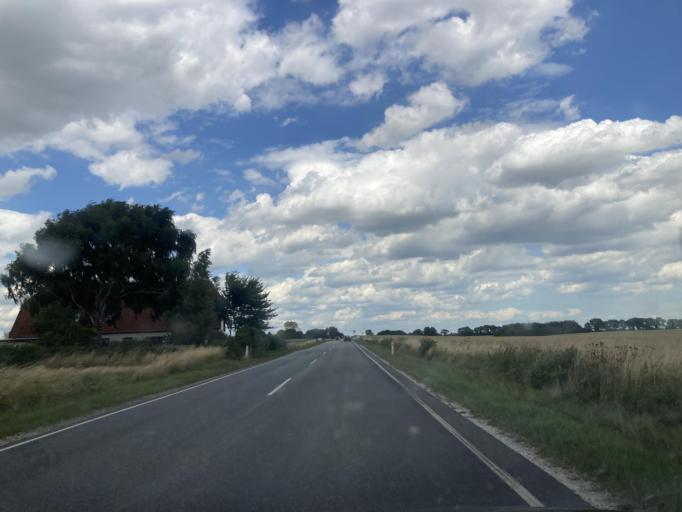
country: DK
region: Zealand
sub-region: Faxe Kommune
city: Haslev
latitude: 55.3353
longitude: 12.0254
